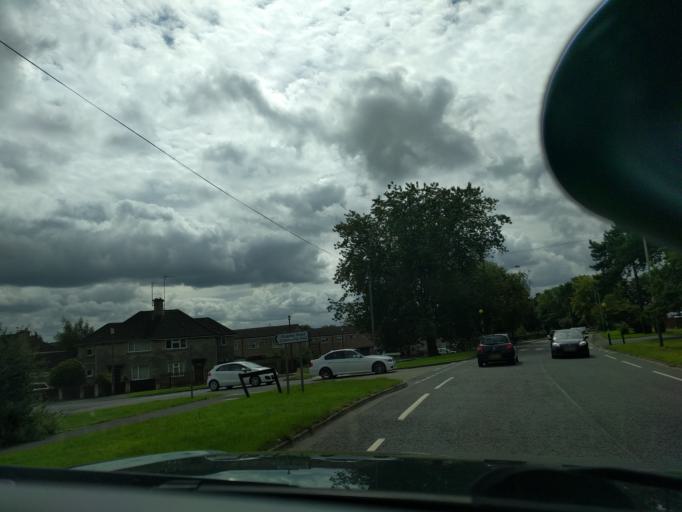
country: GB
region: England
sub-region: Wiltshire
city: Chippenham
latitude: 51.4564
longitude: -2.1376
